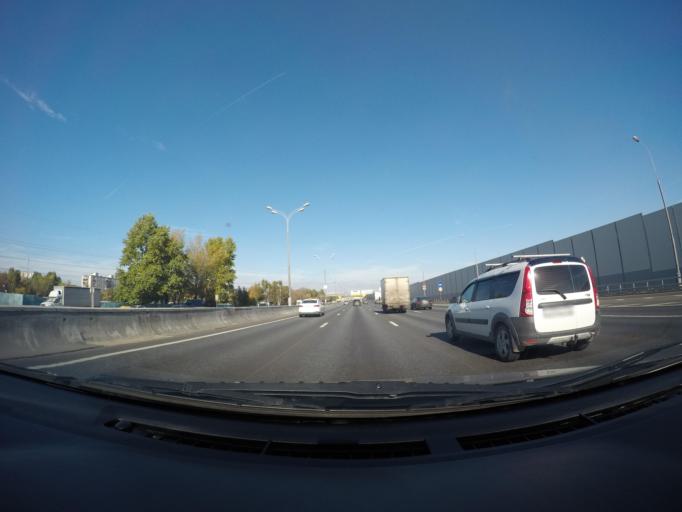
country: RU
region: Moskovskaya
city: Kuskovo
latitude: 55.7334
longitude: 37.8409
